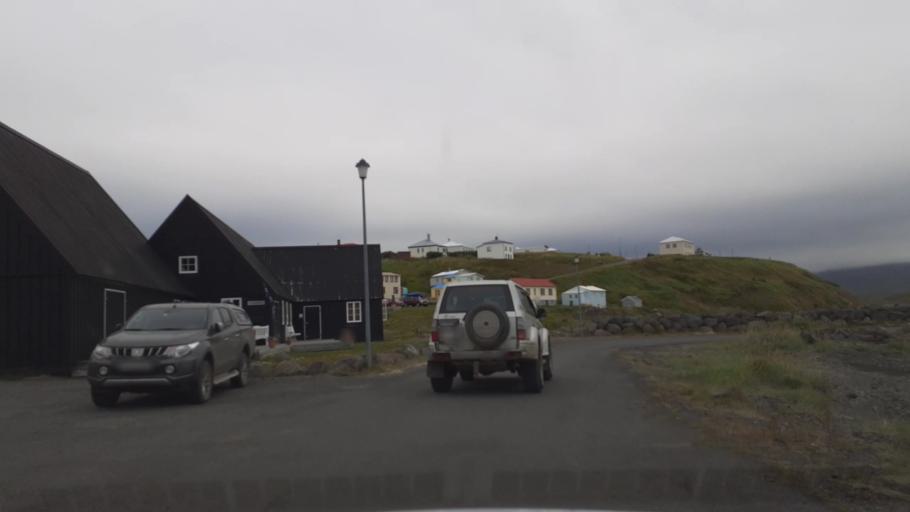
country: IS
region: Northwest
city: Saudarkrokur
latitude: 65.8990
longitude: -19.4194
